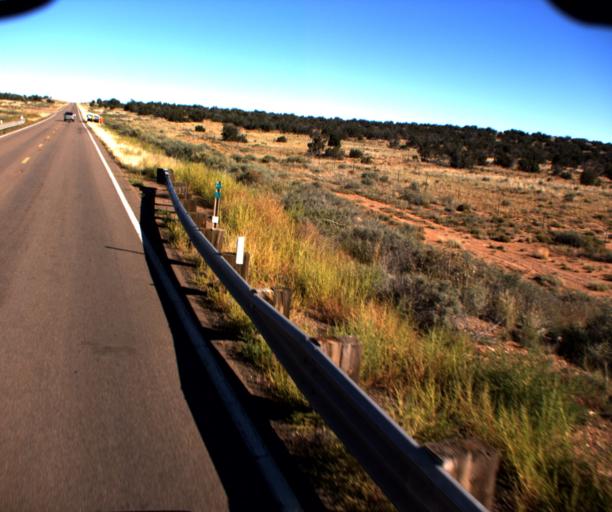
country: US
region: Arizona
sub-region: Navajo County
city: Snowflake
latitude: 34.6131
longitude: -110.0907
